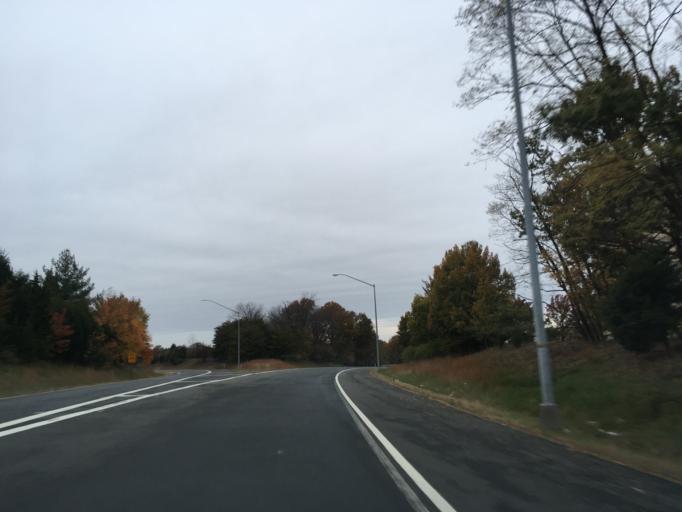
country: US
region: Maryland
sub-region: Baltimore County
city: Woodlawn
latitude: 39.3068
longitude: -76.7389
